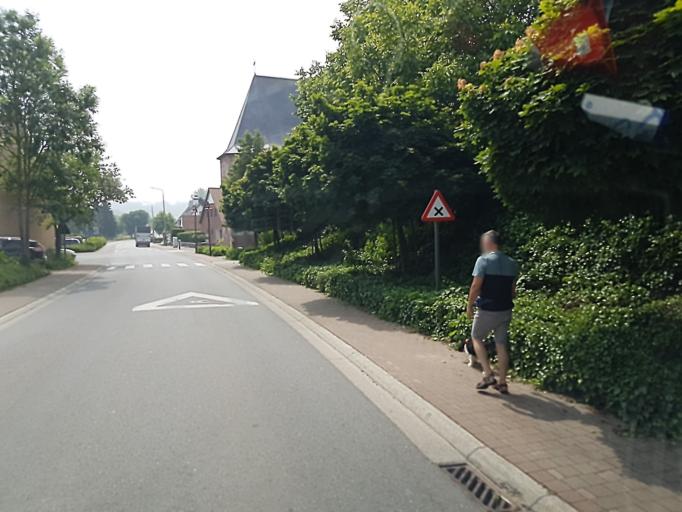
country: BE
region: Flanders
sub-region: Provincie Oost-Vlaanderen
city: Geraardsbergen
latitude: 50.7974
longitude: 3.8990
